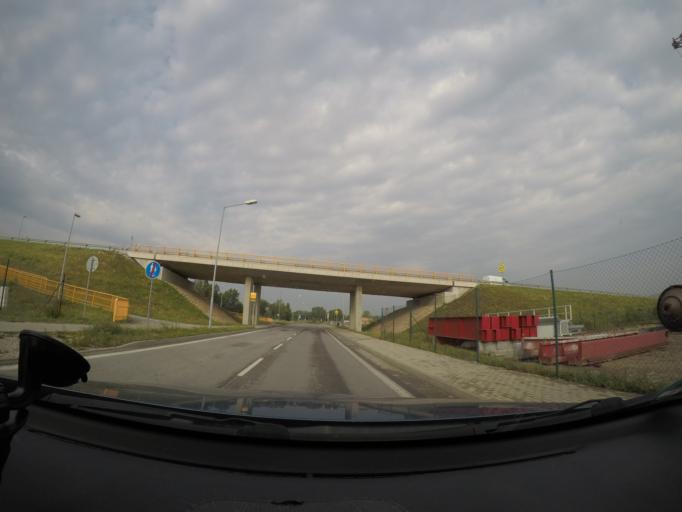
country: SK
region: Trenciansky
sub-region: Okres Trencin
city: Trencin
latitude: 48.8864
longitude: 18.0112
